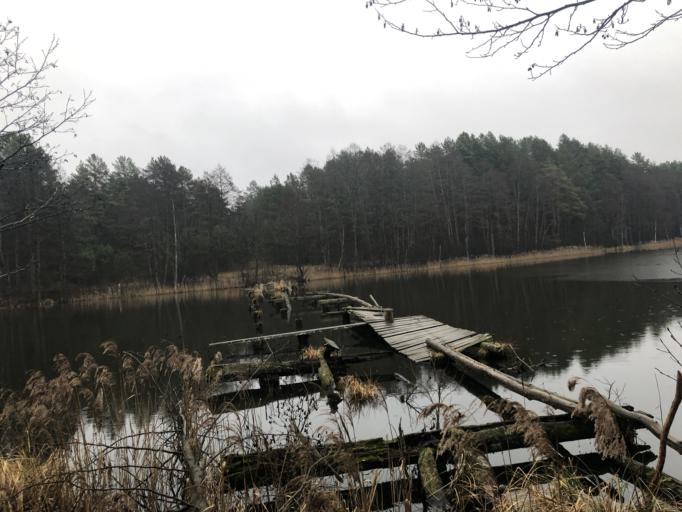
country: LT
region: Alytaus apskritis
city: Druskininkai
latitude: 53.8744
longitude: 24.2117
